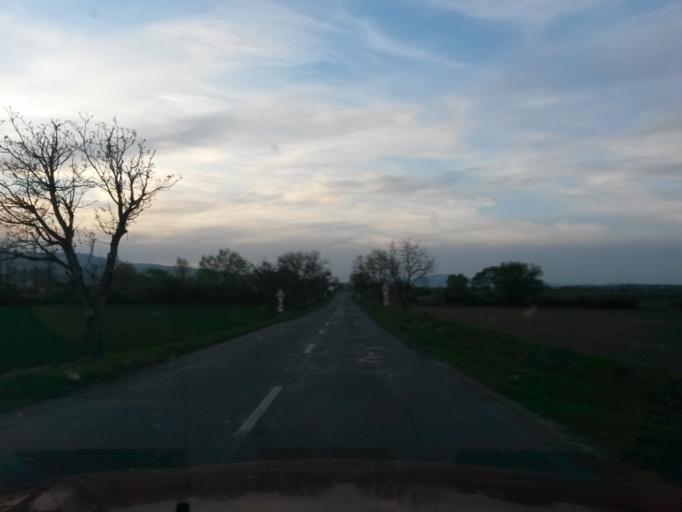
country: HU
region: Borsod-Abauj-Zemplen
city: Satoraljaujhely
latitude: 48.5002
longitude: 21.6290
